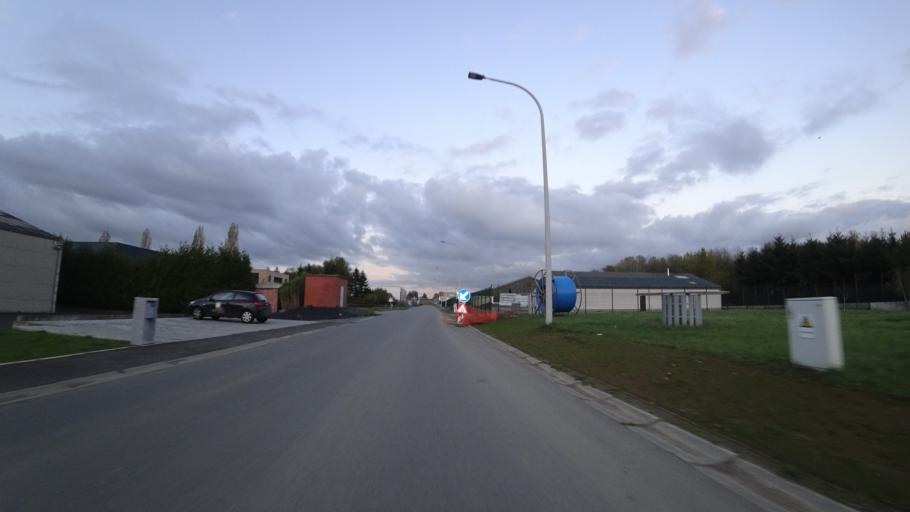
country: BE
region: Wallonia
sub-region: Province de Namur
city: Gembloux
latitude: 50.5776
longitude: 4.7116
